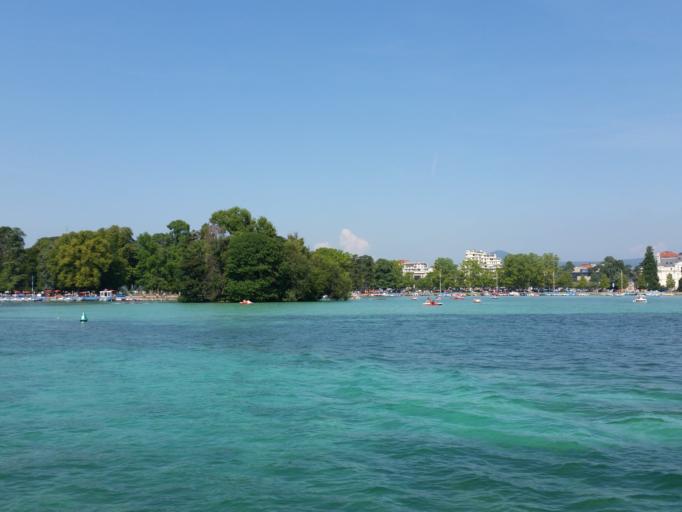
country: FR
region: Rhone-Alpes
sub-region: Departement de la Haute-Savoie
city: Annecy
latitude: 45.8983
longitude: 6.1357
